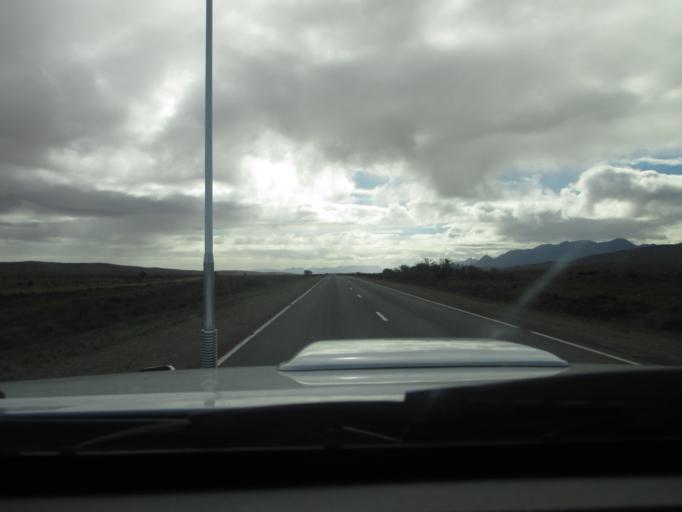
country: AU
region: South Australia
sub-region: Flinders Ranges
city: Quorn
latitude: -31.6281
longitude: 138.3900
